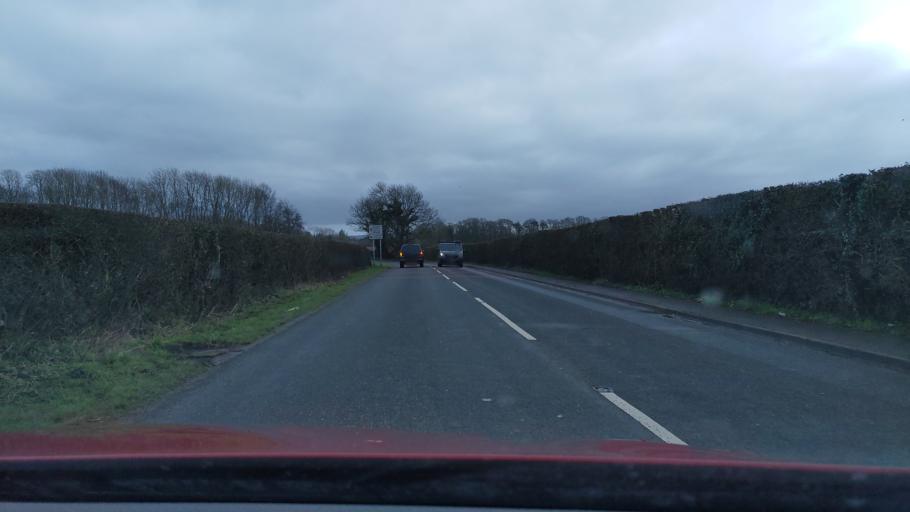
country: GB
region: England
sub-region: Lancashire
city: Tarleton
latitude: 53.6816
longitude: -2.8083
